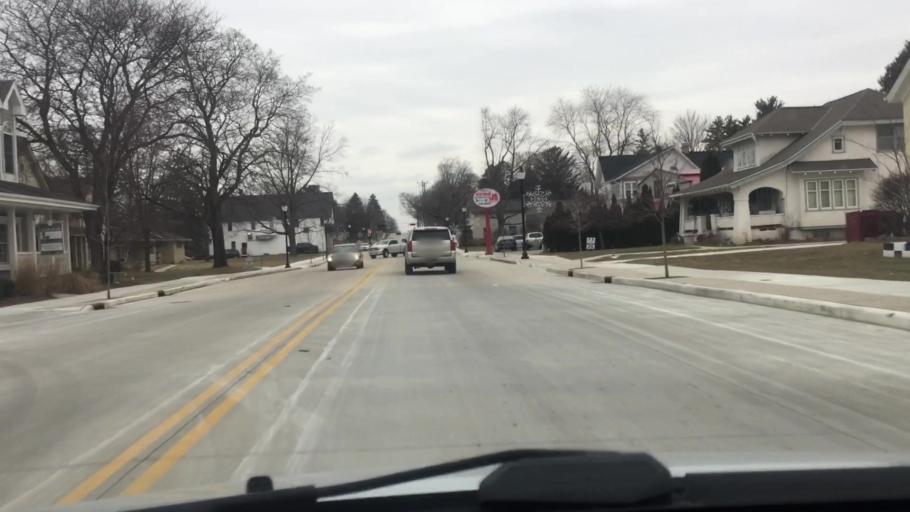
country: US
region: Wisconsin
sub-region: Waukesha County
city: Sussex
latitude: 43.1338
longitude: -88.2210
